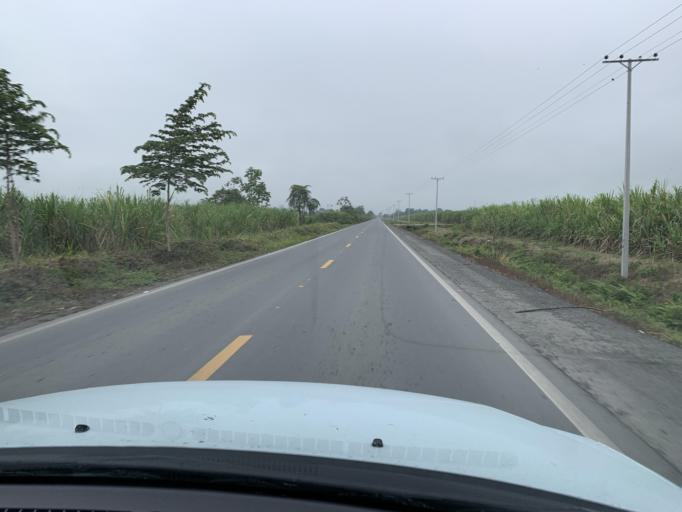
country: EC
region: Guayas
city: Coronel Marcelino Mariduena
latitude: -2.3263
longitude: -79.5226
